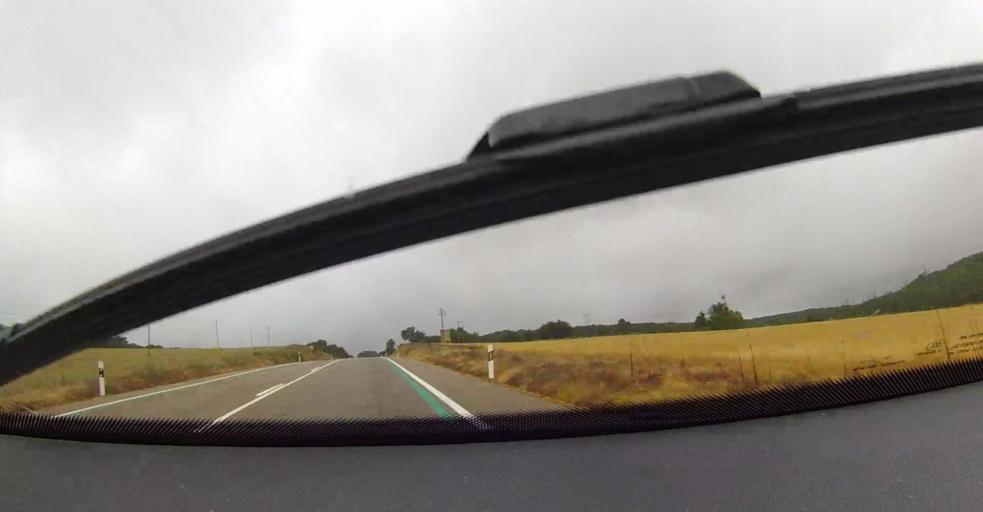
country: ES
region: Castille and Leon
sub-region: Provincia de Palencia
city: Saldana
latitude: 42.5554
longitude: -4.7386
